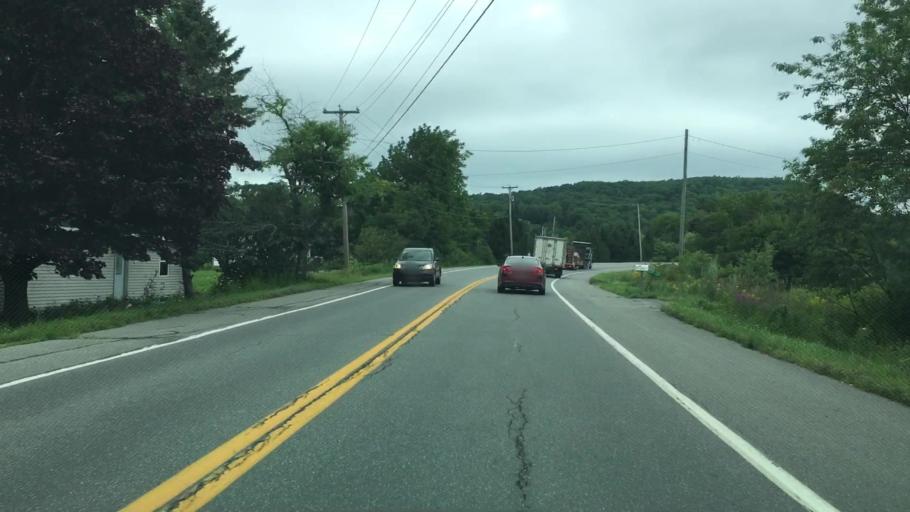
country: US
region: Maine
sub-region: Waldo County
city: Frankfort
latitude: 44.5657
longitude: -68.8674
